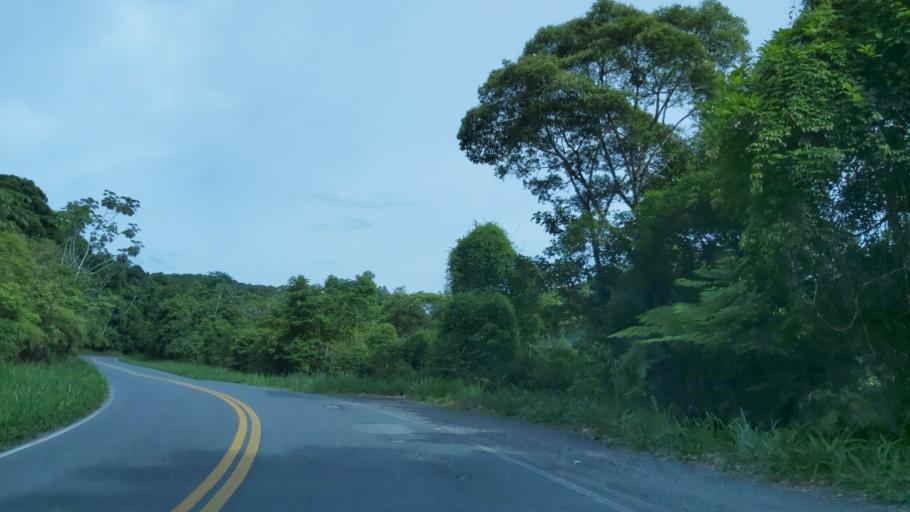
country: BR
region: Sao Paulo
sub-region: Juquia
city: Juquia
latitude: -24.1058
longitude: -47.6251
